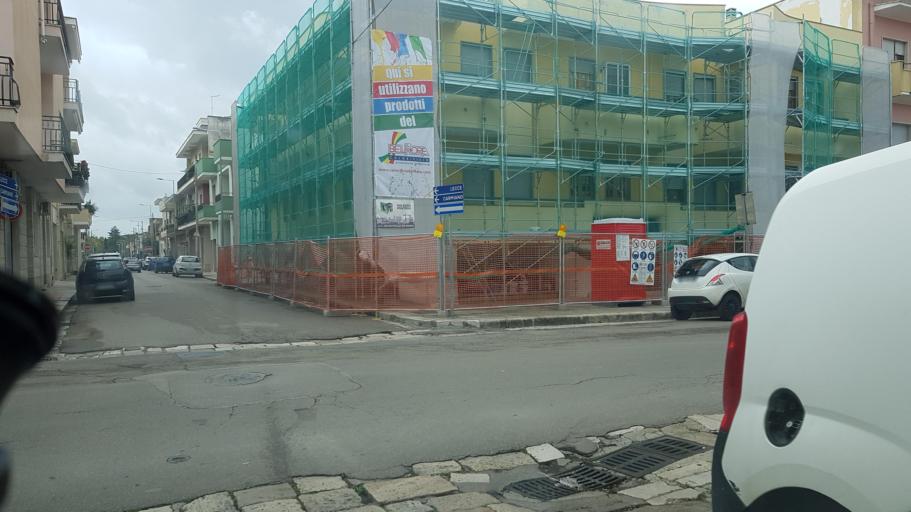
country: IT
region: Apulia
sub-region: Provincia di Lecce
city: Novoli
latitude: 40.3751
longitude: 18.0464
